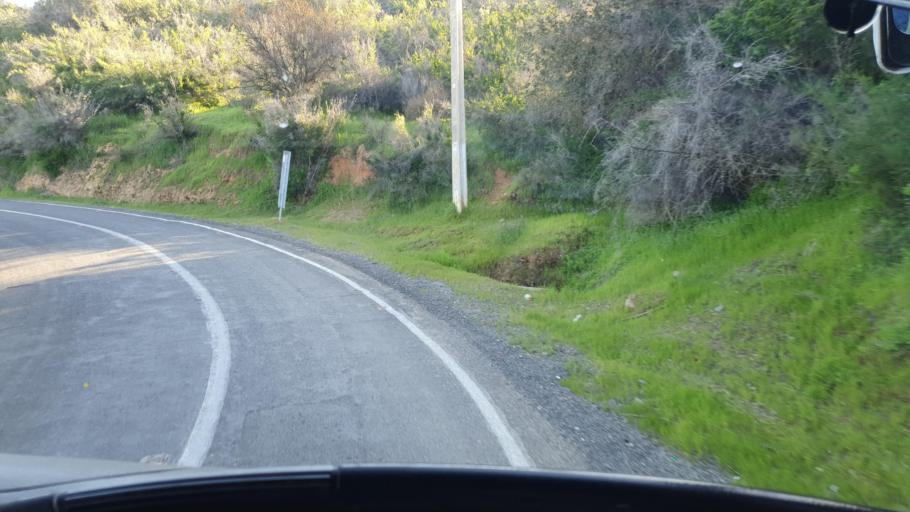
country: CL
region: Valparaiso
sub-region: Provincia de Marga Marga
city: Limache
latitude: -33.1973
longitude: -71.2213
